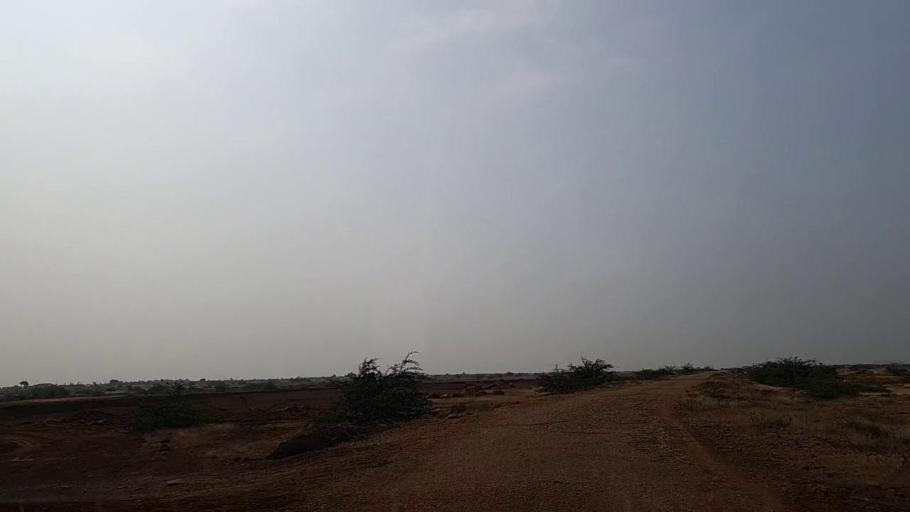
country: PK
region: Sindh
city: Thatta
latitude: 24.7362
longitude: 67.8392
